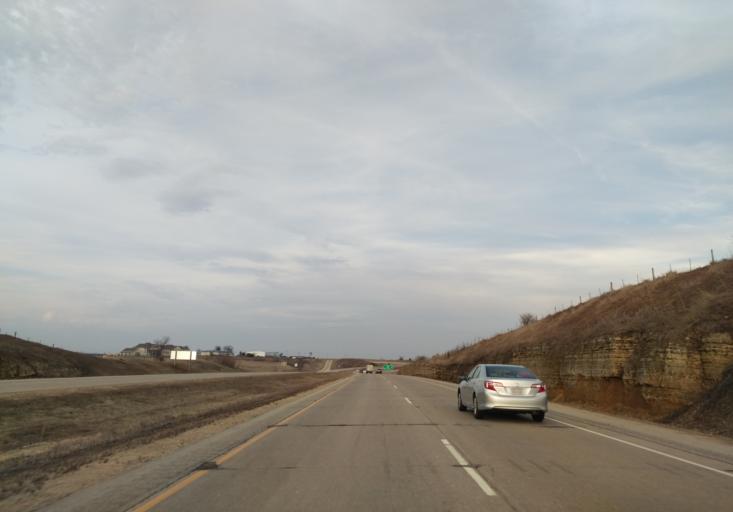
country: US
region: Wisconsin
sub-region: Dane County
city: Mount Horeb
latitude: 43.0004
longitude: -89.7120
